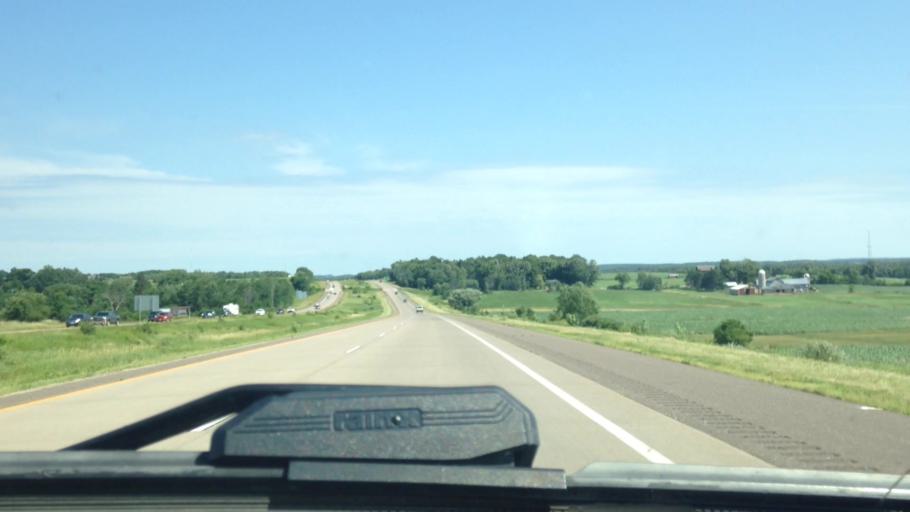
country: US
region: Wisconsin
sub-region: Barron County
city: Rice Lake
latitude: 45.5240
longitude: -91.7594
